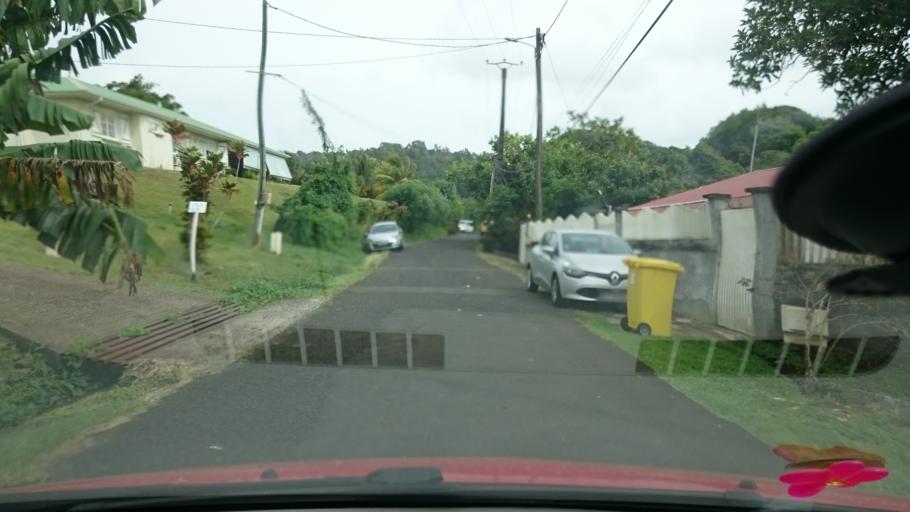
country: MQ
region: Martinique
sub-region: Martinique
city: Riviere-Pilote
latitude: 14.4987
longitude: -60.9139
